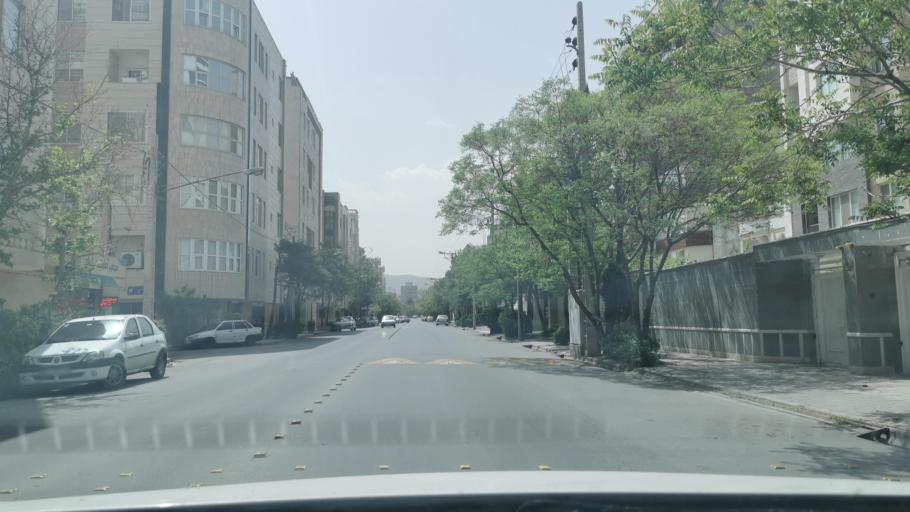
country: IR
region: Razavi Khorasan
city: Mashhad
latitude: 36.3386
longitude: 59.4827
